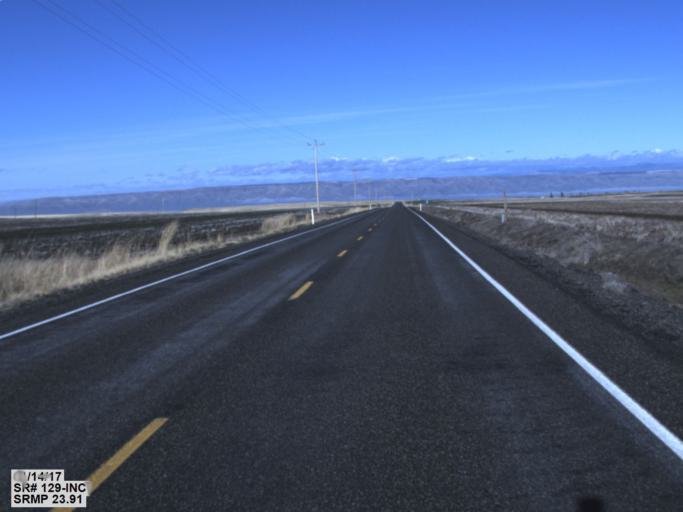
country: US
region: Washington
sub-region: Asotin County
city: Asotin
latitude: 46.2114
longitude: -117.0703
